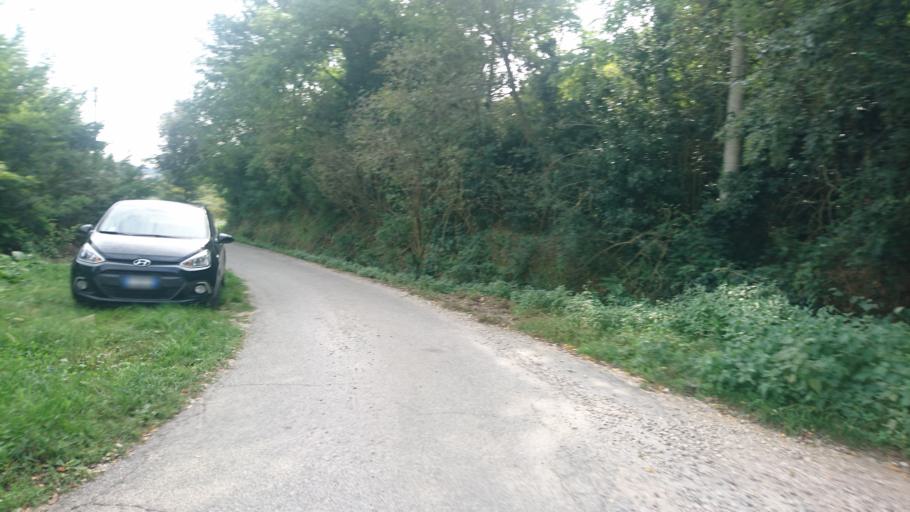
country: IT
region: Veneto
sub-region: Provincia di Padova
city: Arqua Petrarca
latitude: 45.2867
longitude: 11.7248
